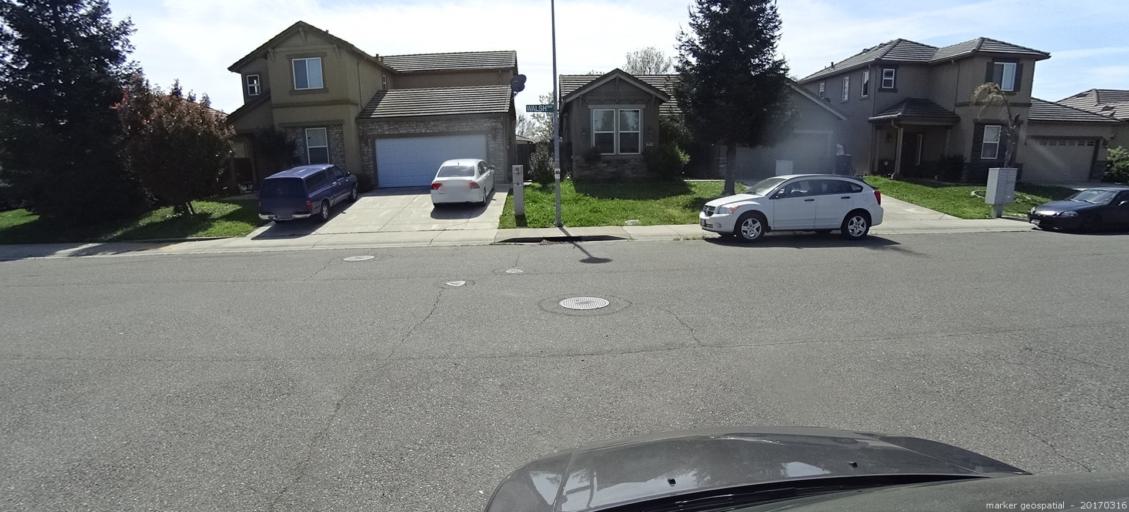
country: US
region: California
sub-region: Sacramento County
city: Parkway
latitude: 38.4783
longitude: -121.4888
